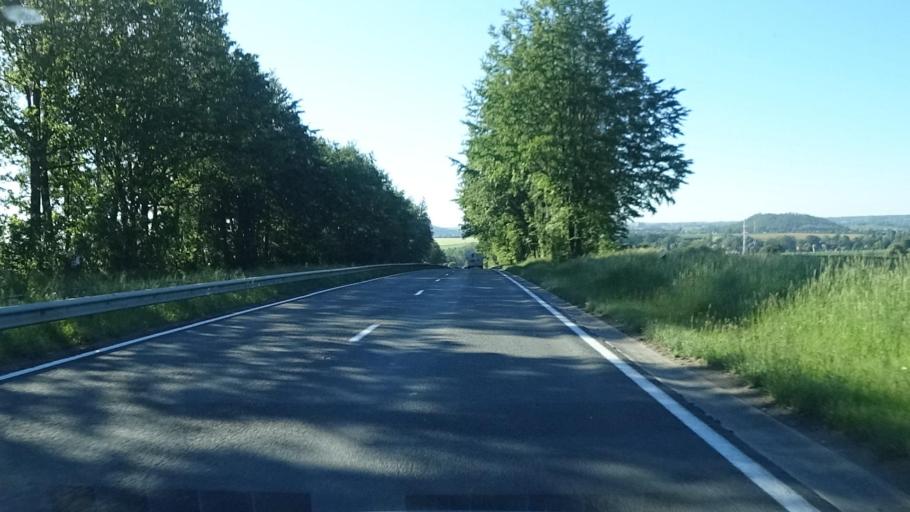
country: BE
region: Wallonia
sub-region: Province du Hainaut
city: La Louviere
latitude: 50.4605
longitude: 4.1444
